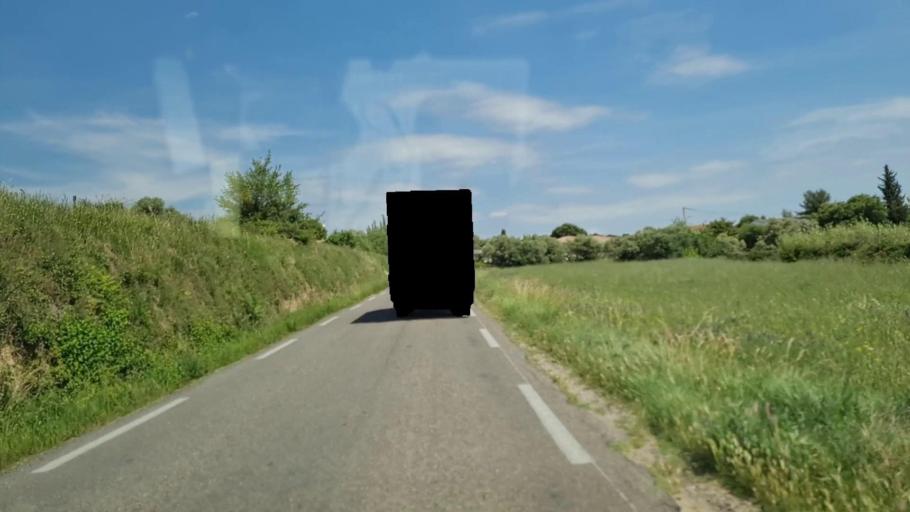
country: FR
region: Languedoc-Roussillon
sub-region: Departement du Gard
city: Cabrieres
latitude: 43.8973
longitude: 4.4728
